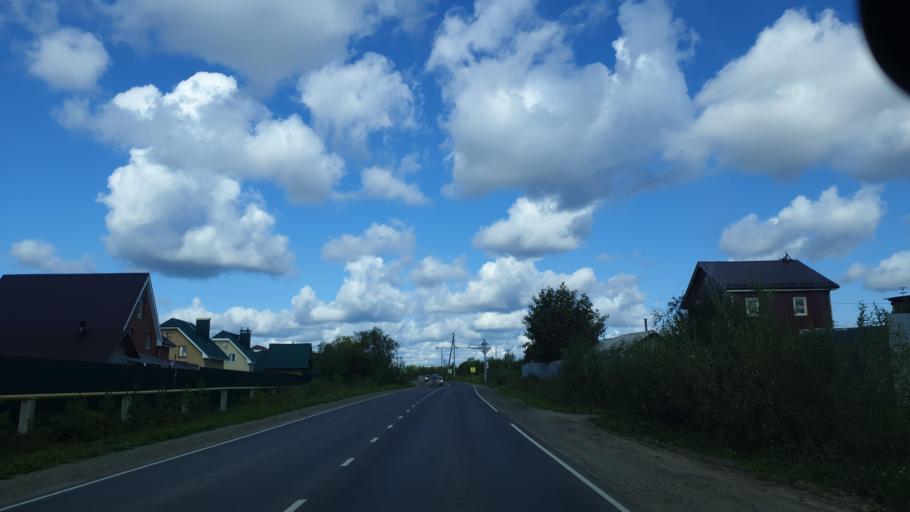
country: RU
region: Komi Republic
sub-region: Syktyvdinskiy Rayon
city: Syktyvkar
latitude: 61.6372
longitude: 50.8026
